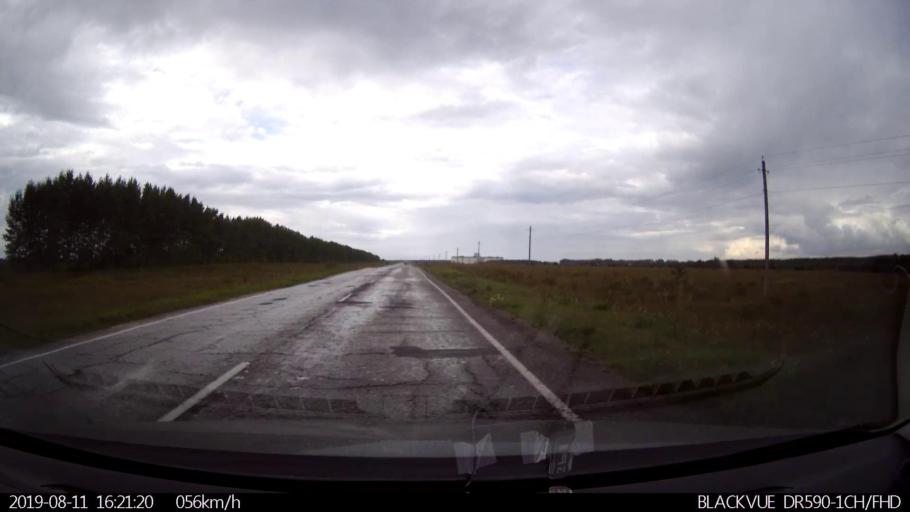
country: RU
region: Ulyanovsk
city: Mayna
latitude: 54.0791
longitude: 47.5984
